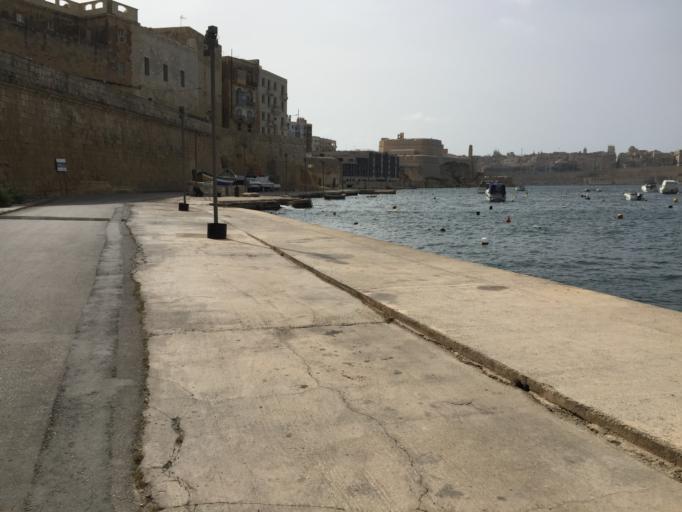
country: MT
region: Bormla
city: Cospicua
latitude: 35.8891
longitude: 14.5233
